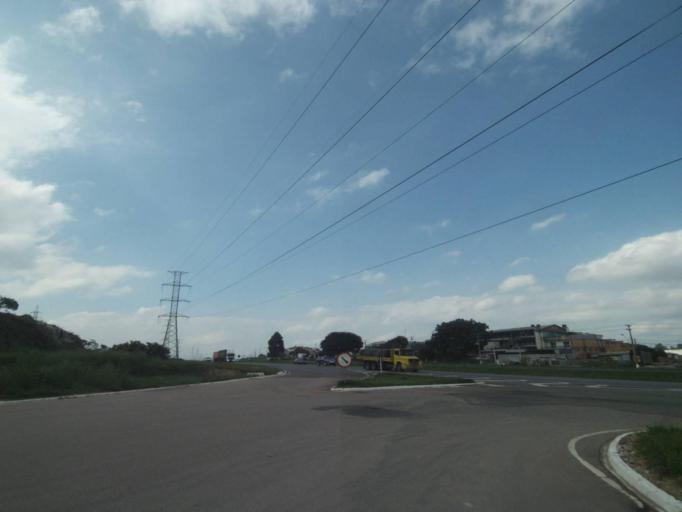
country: BR
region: Parana
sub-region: Curitiba
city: Curitiba
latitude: -25.5096
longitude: -49.3399
